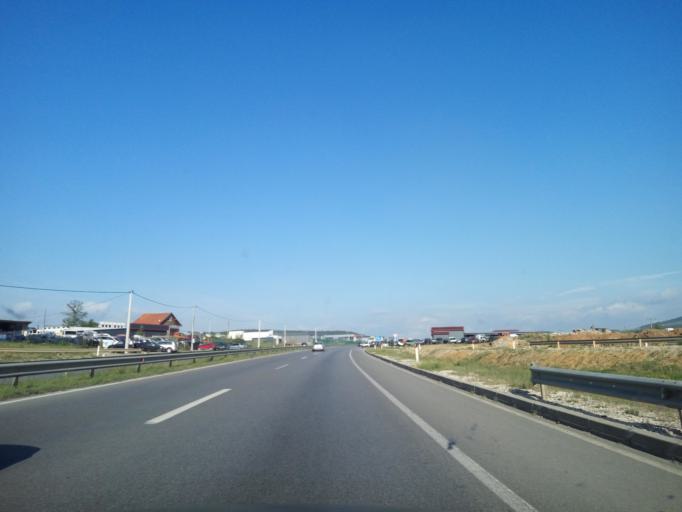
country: XK
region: Pristina
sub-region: Komuna e Drenasit
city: Glogovac
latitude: 42.6026
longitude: 20.9537
